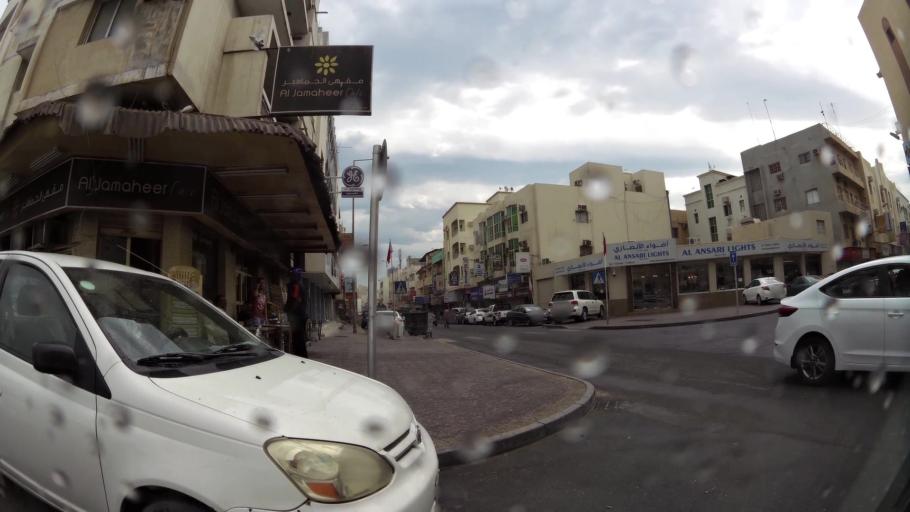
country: BH
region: Manama
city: Manama
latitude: 26.2294
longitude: 50.5895
